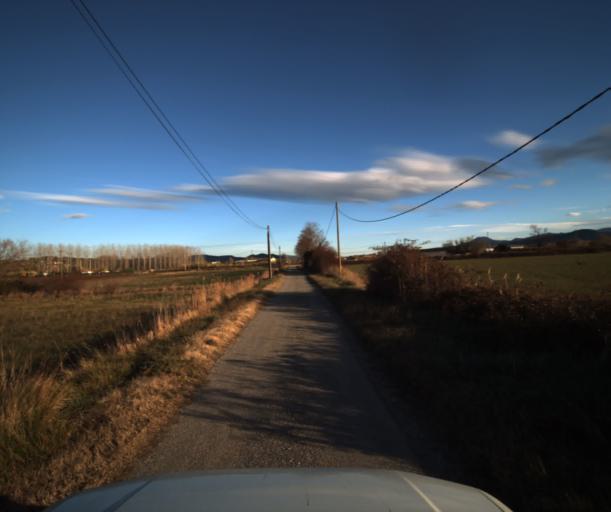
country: FR
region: Provence-Alpes-Cote d'Azur
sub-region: Departement du Vaucluse
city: Pertuis
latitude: 43.6815
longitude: 5.4900
